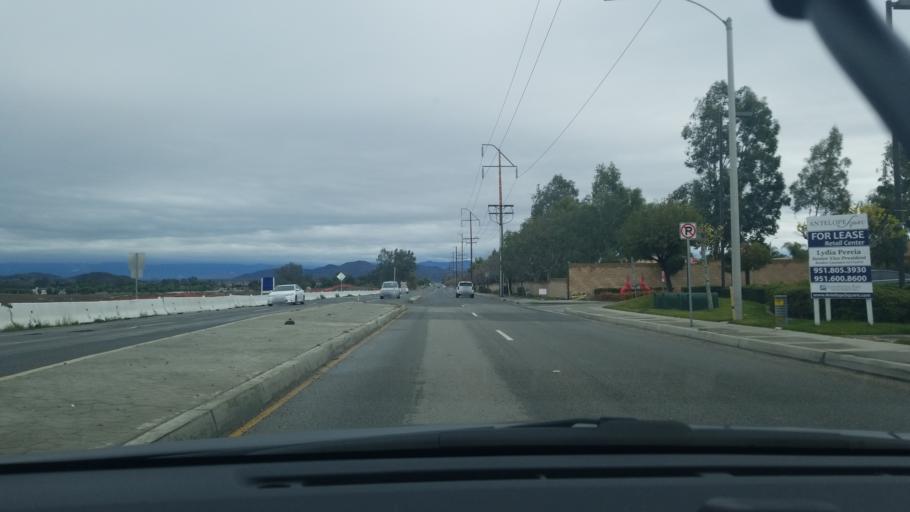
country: US
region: California
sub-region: Riverside County
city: Sun City
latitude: 33.6415
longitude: -117.1671
